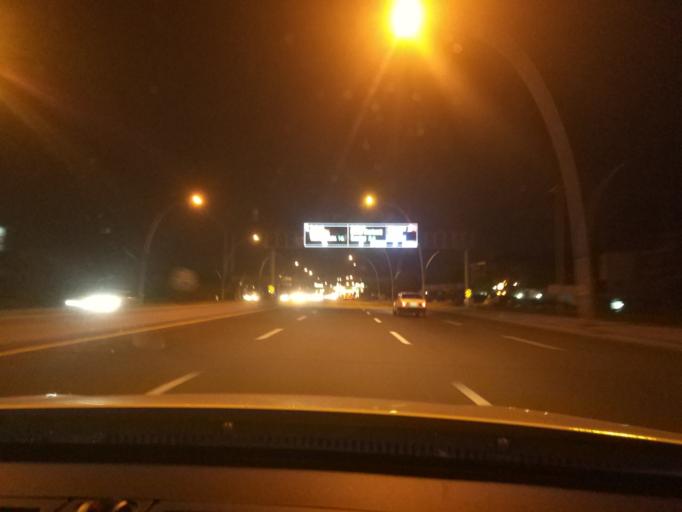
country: TR
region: Ankara
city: Mamak
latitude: 40.0730
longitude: 32.9444
